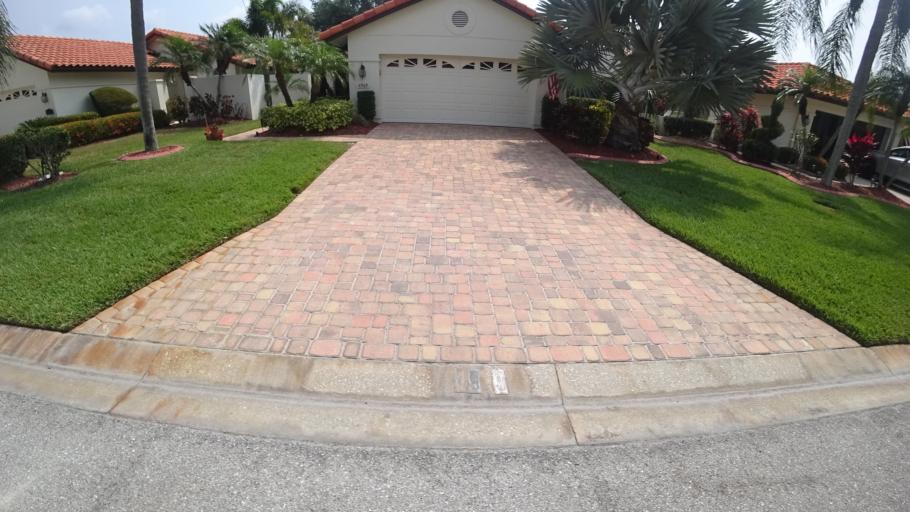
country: US
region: Florida
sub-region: Manatee County
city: Samoset
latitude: 27.4535
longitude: -82.5131
